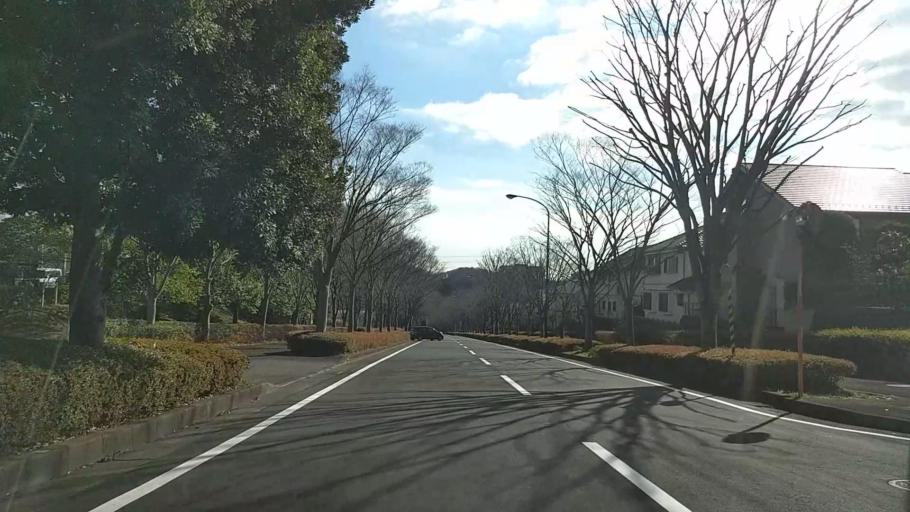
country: JP
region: Kanagawa
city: Atsugi
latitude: 35.4524
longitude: 139.3060
